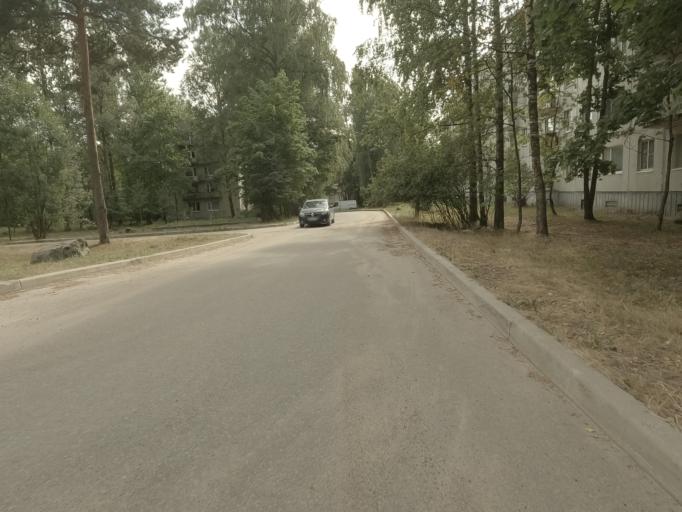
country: RU
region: Leningrad
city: Kamennogorsk
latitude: 60.9552
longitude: 29.1326
